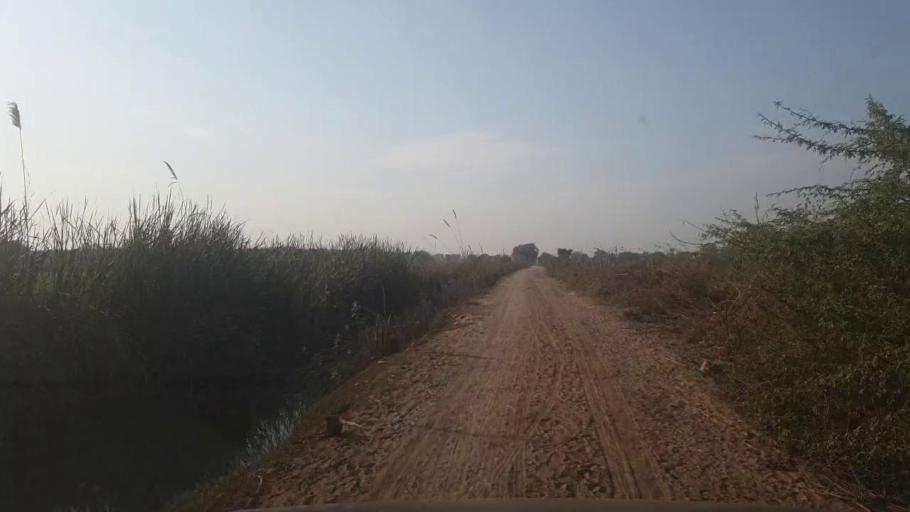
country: PK
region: Sindh
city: Sakrand
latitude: 26.0632
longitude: 68.3469
